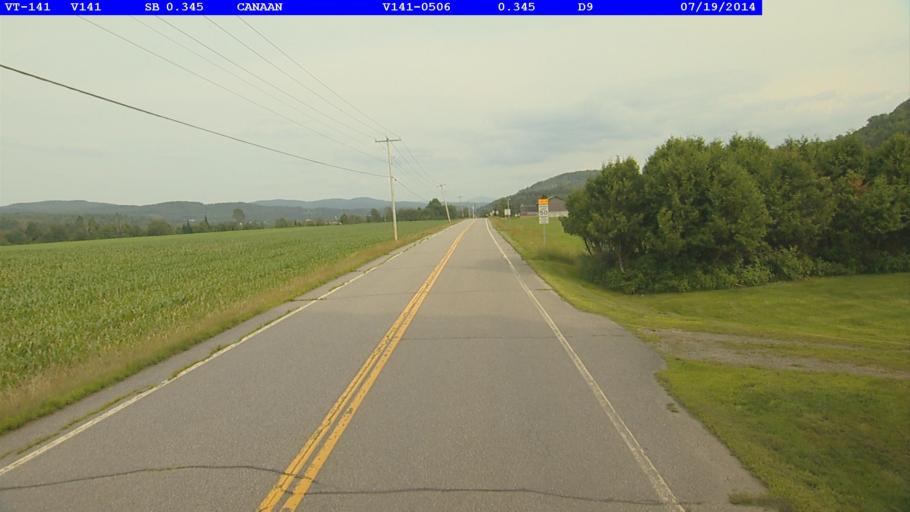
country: US
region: New Hampshire
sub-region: Coos County
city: Colebrook
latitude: 45.0110
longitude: -71.5589
